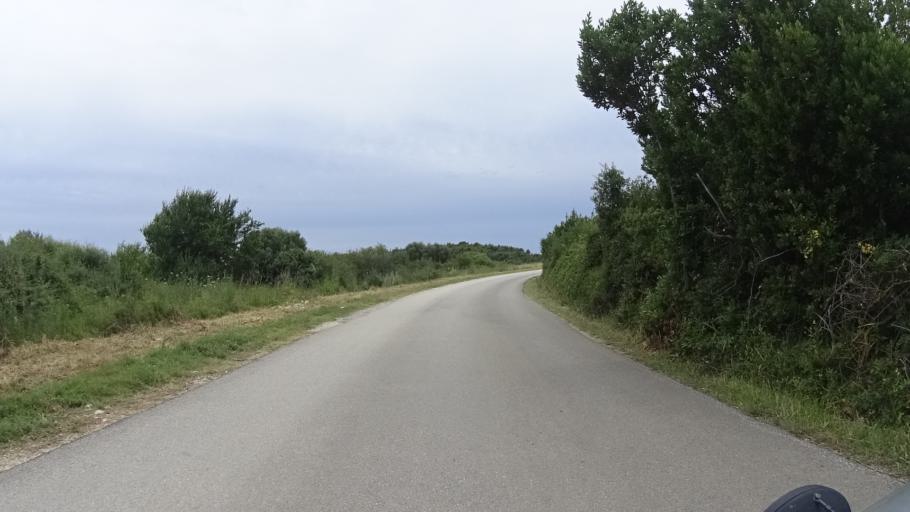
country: HR
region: Istarska
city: Medulin
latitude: 44.8011
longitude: 13.9063
